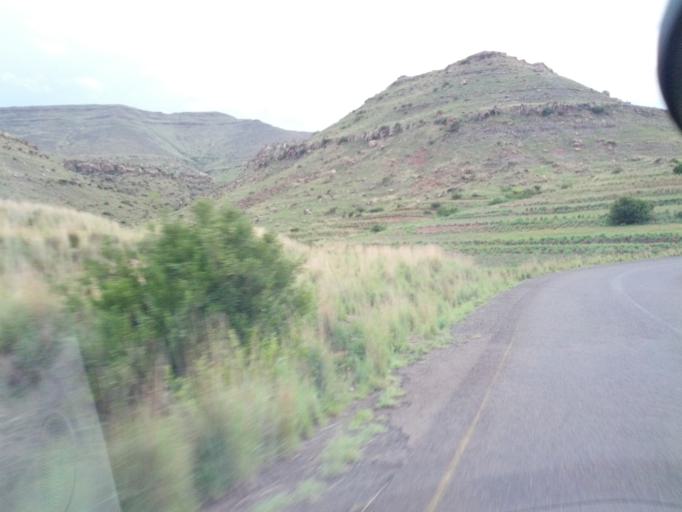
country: LS
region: Qacha's Nek
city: Qacha's Nek
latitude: -30.0671
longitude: 28.5495
